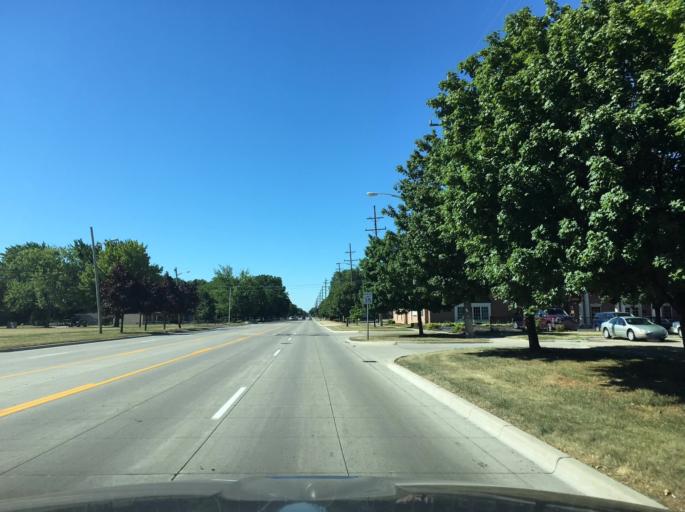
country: US
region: Michigan
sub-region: Macomb County
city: Saint Clair Shores
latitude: 42.5091
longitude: -82.9085
